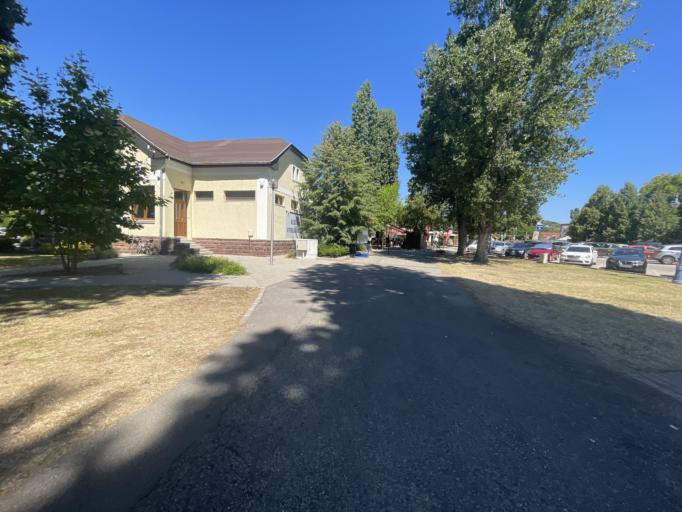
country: HU
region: Veszprem
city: Csopak
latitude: 46.9847
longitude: 17.9792
